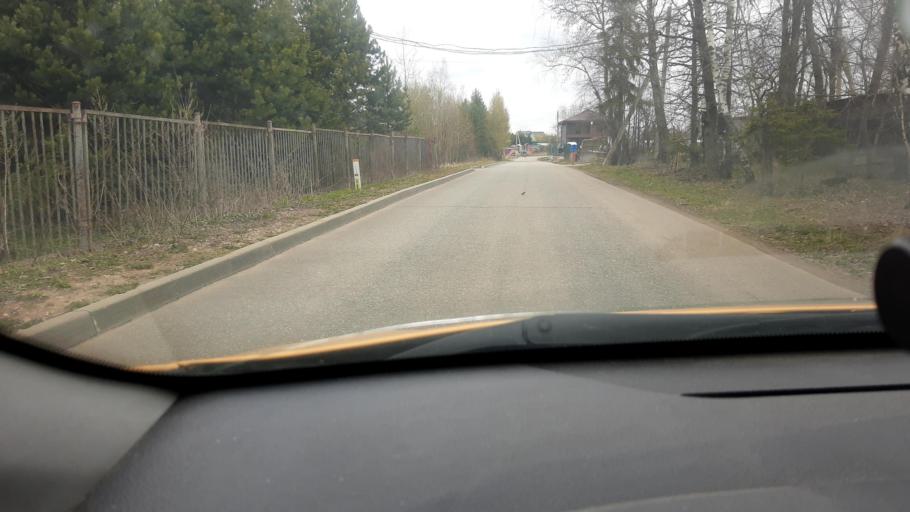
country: RU
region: Moskovskaya
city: Povarovo
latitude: 56.0215
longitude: 36.9905
